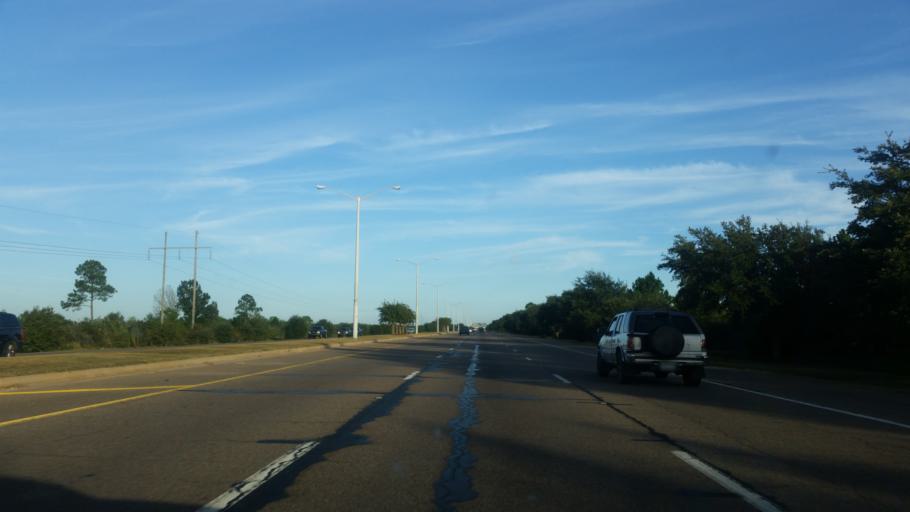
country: US
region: Mississippi
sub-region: Jackson County
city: Gautier
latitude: 30.3785
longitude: -88.5898
